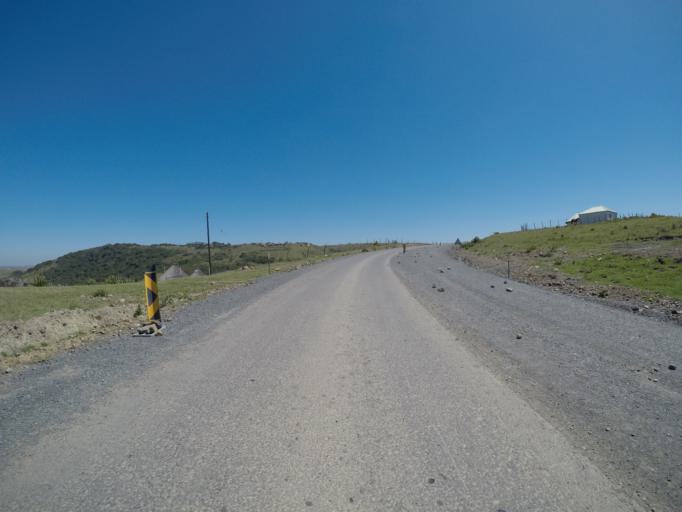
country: ZA
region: Eastern Cape
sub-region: OR Tambo District Municipality
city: Libode
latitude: -32.0048
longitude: 29.1160
